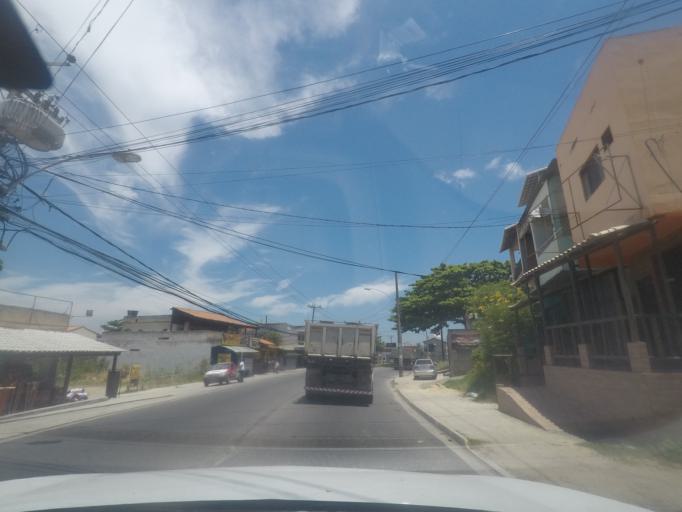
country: BR
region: Rio de Janeiro
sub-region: Itaguai
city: Itaguai
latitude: -22.9300
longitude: -43.6892
